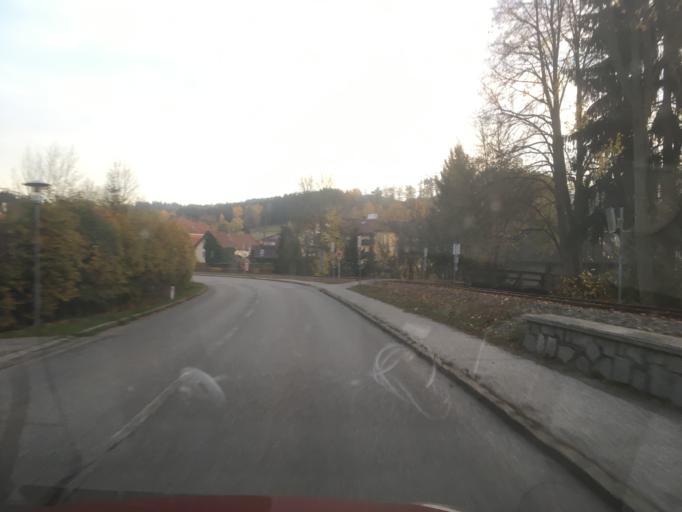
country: AT
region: Lower Austria
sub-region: Politischer Bezirk Zwettl
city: Langschlag
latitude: 48.5756
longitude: 14.8855
